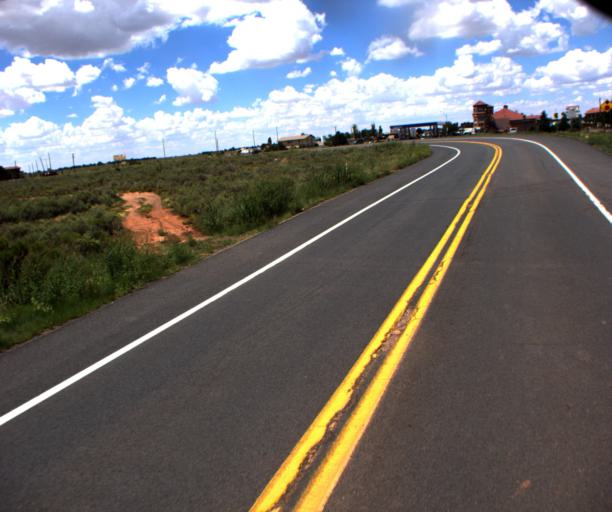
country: US
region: Arizona
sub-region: Coconino County
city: Grand Canyon Village
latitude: 35.6511
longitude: -112.1369
